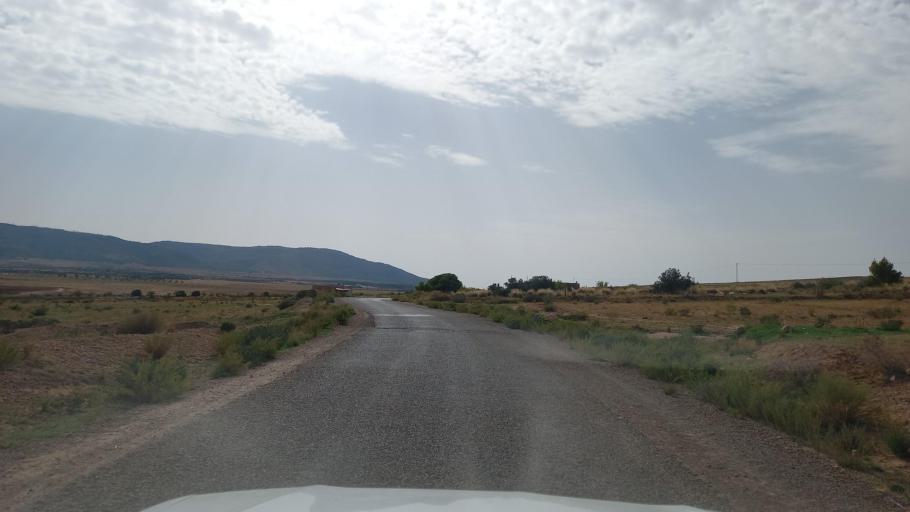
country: TN
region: Al Qasrayn
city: Kasserine
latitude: 35.3624
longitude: 8.8472
